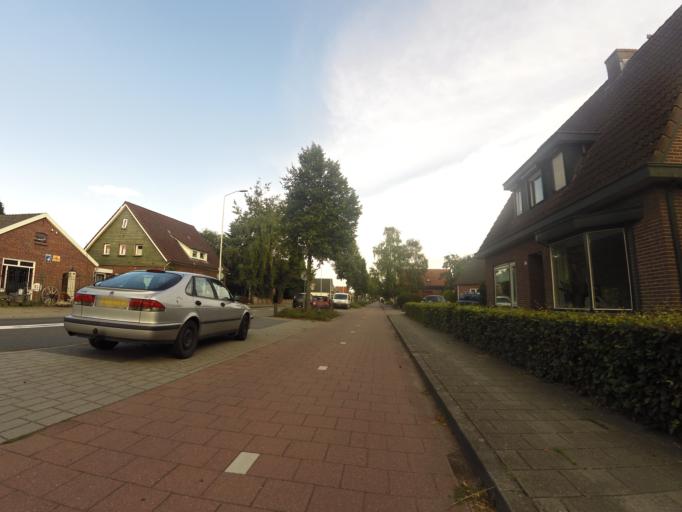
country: NL
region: Gelderland
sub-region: Oude IJsselstreek
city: Gendringen
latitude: 51.9281
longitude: 6.3483
